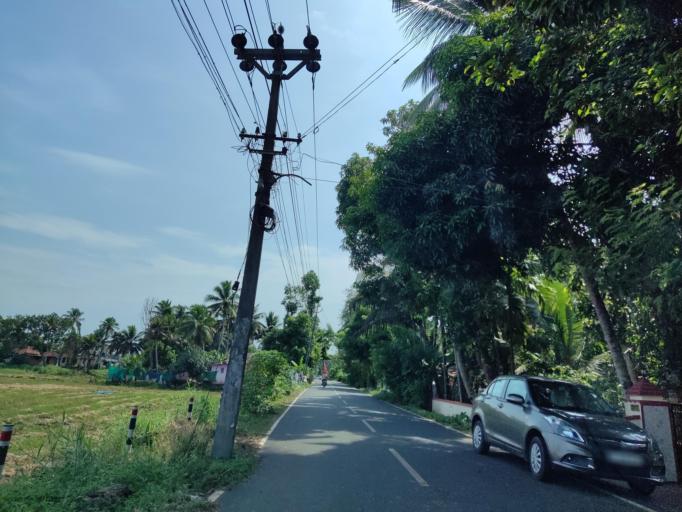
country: IN
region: Kerala
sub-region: Alappuzha
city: Mavelikara
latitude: 9.3268
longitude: 76.4718
